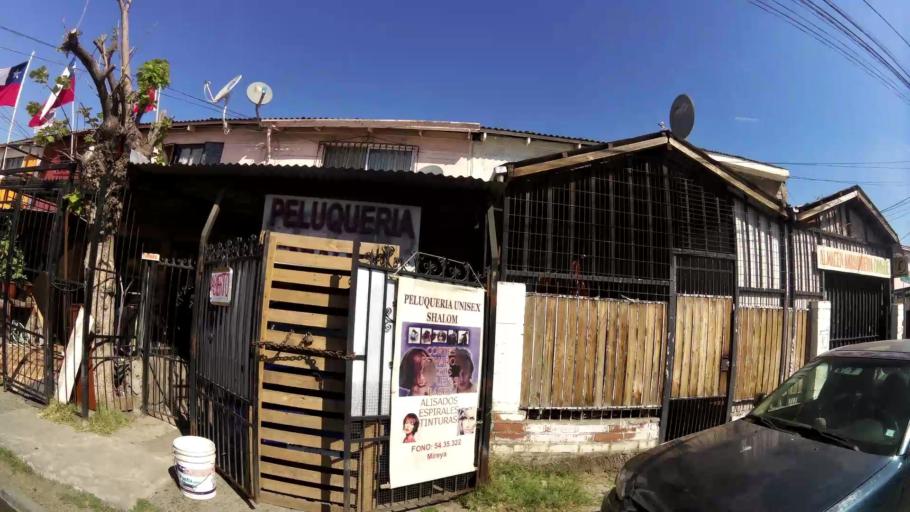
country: CL
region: Santiago Metropolitan
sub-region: Provincia de Santiago
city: La Pintana
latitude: -33.5607
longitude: -70.6205
